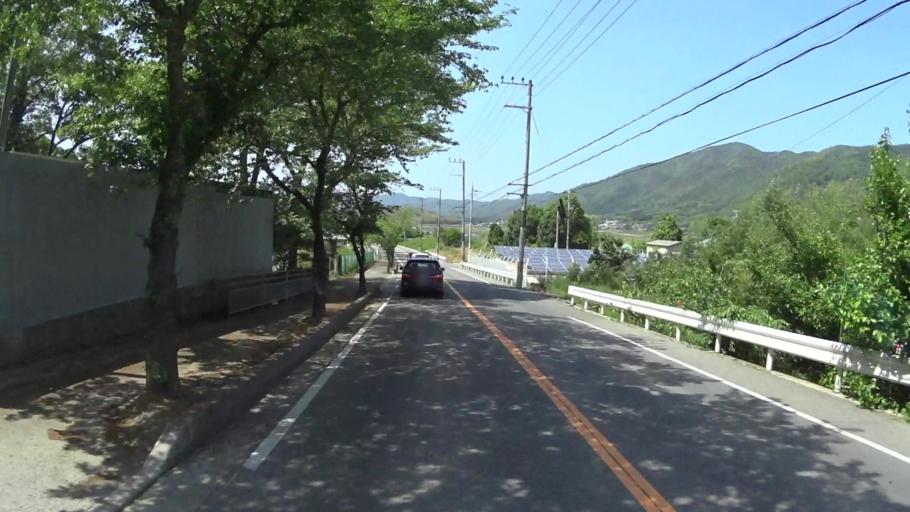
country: JP
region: Kyoto
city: Kameoka
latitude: 35.0475
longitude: 135.5756
